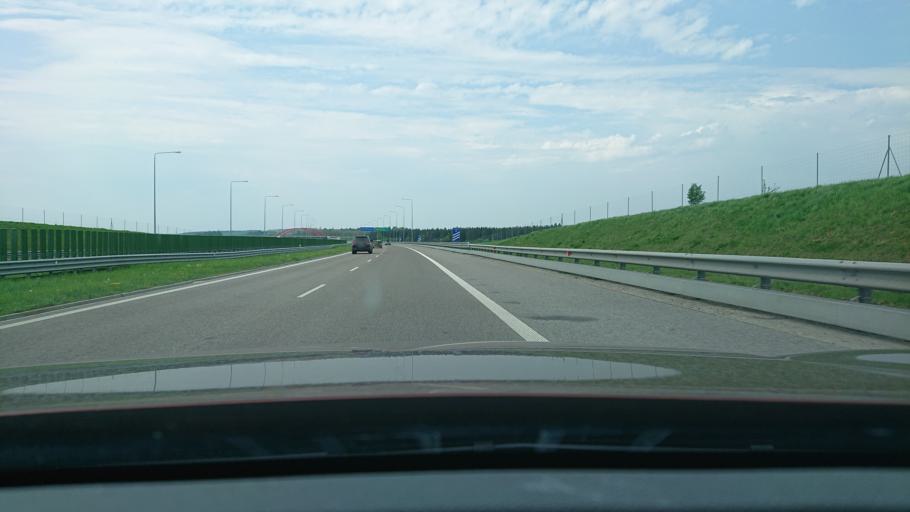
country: PL
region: Subcarpathian Voivodeship
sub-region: Powiat jaroslawski
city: Pawlosiow
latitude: 49.9667
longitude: 22.6541
